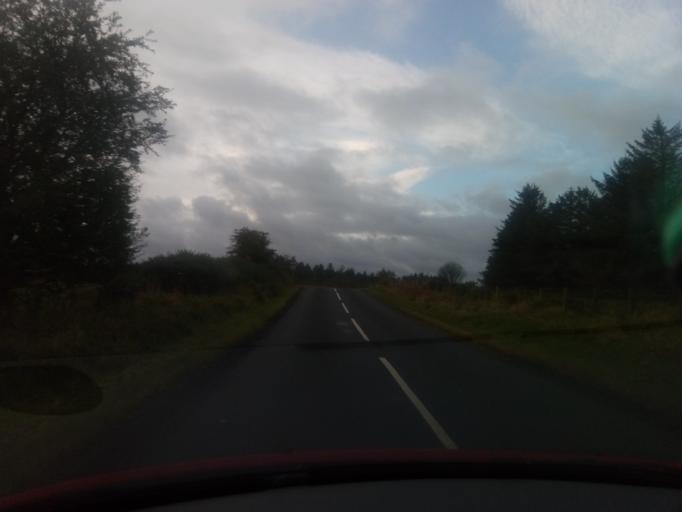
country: GB
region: Scotland
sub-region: The Scottish Borders
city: Jedburgh
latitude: 55.4392
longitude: -2.5958
